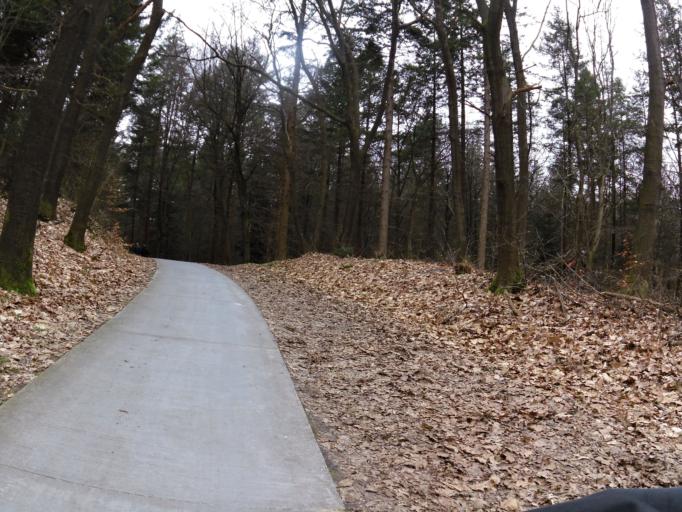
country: NL
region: Drenthe
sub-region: Gemeente Westerveld
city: Dwingeloo
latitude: 52.9470
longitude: 6.3308
